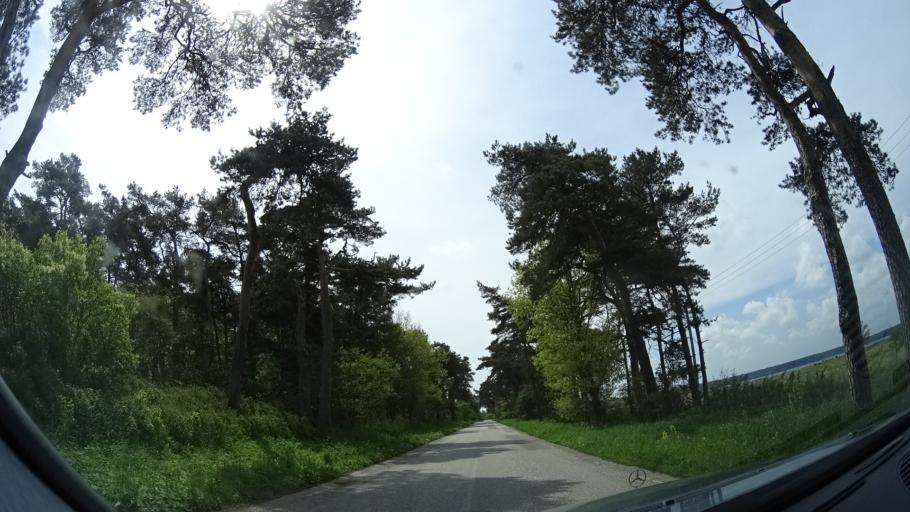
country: SE
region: Skane
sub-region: Sjobo Kommun
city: Sjoebo
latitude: 55.6770
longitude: 13.6267
